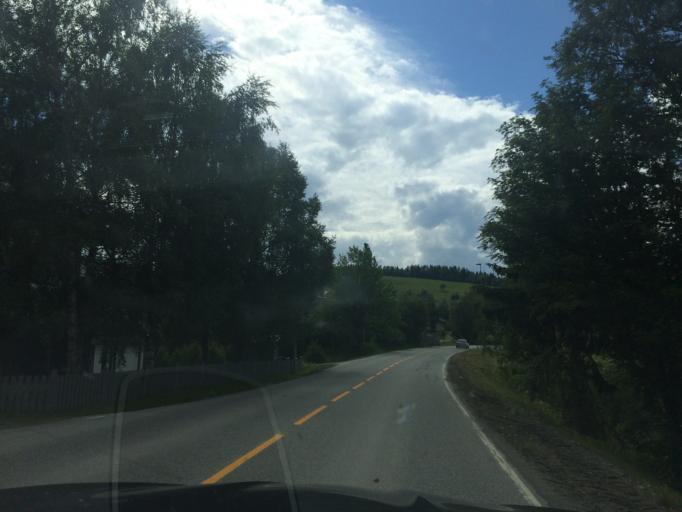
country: NO
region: Sor-Trondelag
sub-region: Selbu
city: Mebonden
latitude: 63.2418
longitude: 11.0847
